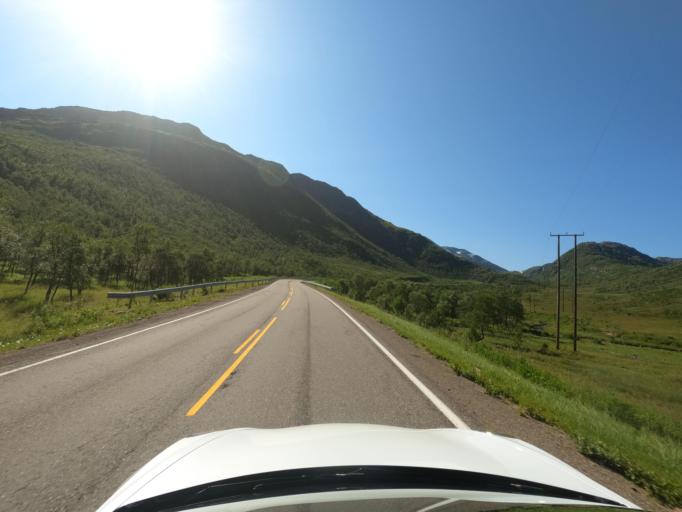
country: NO
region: Nordland
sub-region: Lodingen
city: Lodingen
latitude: 68.4954
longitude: 15.6995
